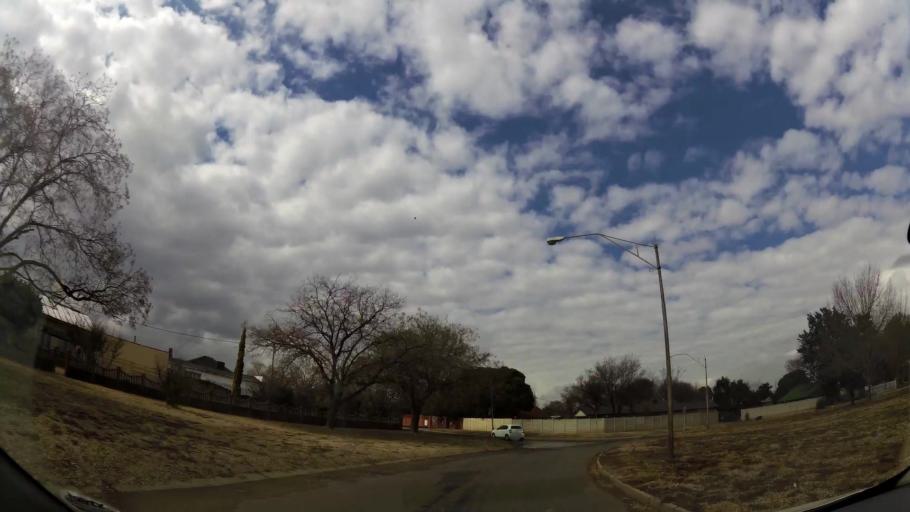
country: ZA
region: Gauteng
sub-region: Sedibeng District Municipality
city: Vereeniging
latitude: -26.6537
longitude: 27.9913
